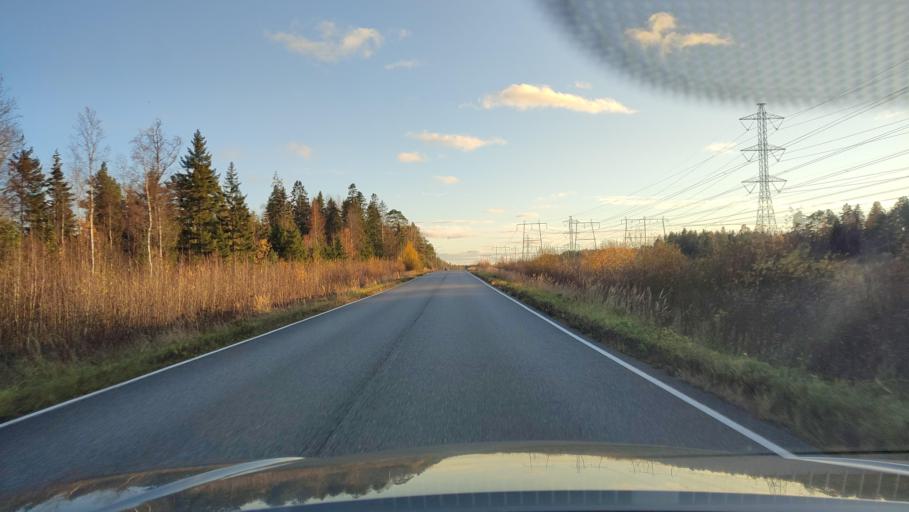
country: FI
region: Ostrobothnia
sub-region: Sydosterbotten
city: Kristinestad
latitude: 62.2800
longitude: 21.3498
